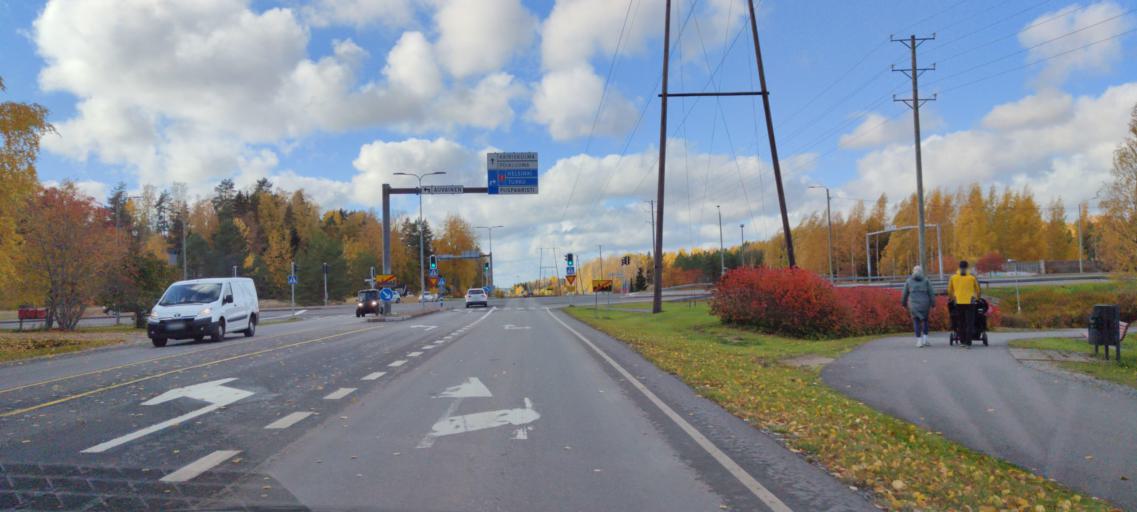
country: FI
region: Varsinais-Suomi
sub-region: Turku
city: Kaarina
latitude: 60.4064
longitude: 22.3445
